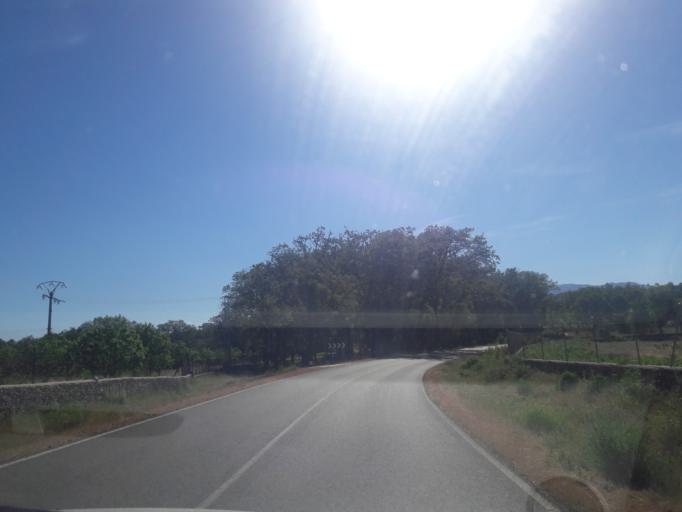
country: ES
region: Castille and Leon
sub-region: Provincia de Salamanca
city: Lagunilla
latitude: 40.3264
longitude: -5.9467
